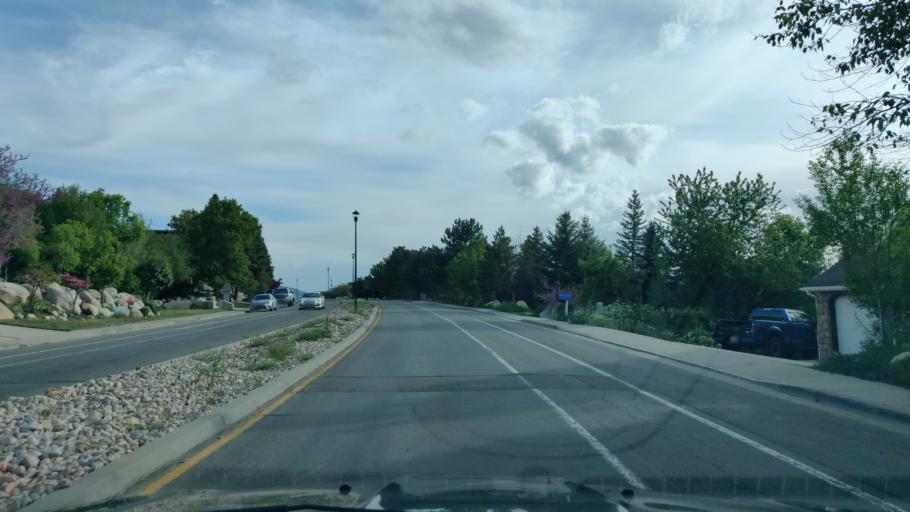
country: US
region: Utah
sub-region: Salt Lake County
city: Granite
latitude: 40.5679
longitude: -111.8026
